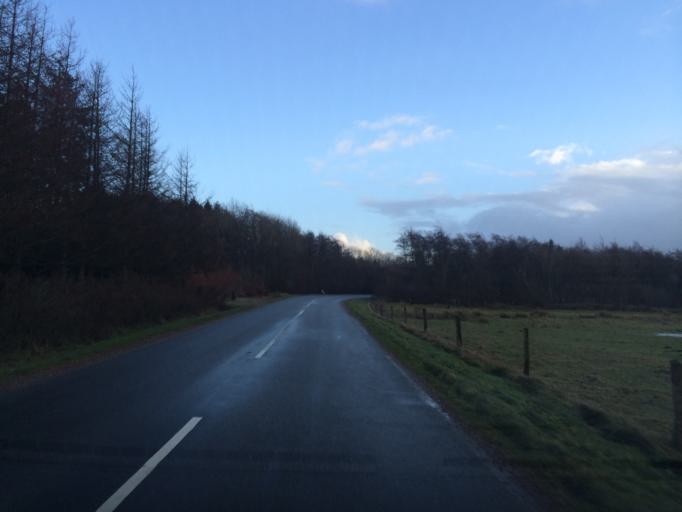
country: DK
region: Central Jutland
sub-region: Holstebro Kommune
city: Ulfborg
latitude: 56.2462
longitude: 8.3807
